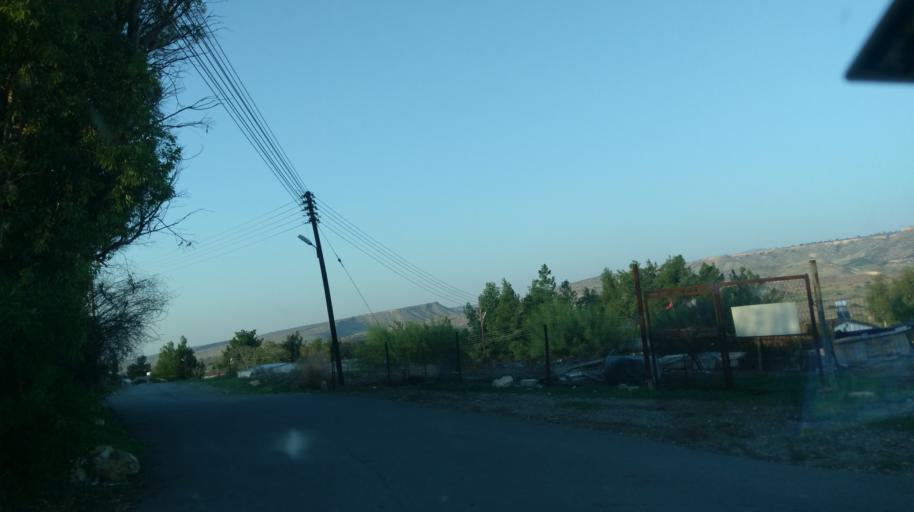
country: CY
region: Lefkosia
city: Astromeritis
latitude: 35.2023
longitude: 33.0600
